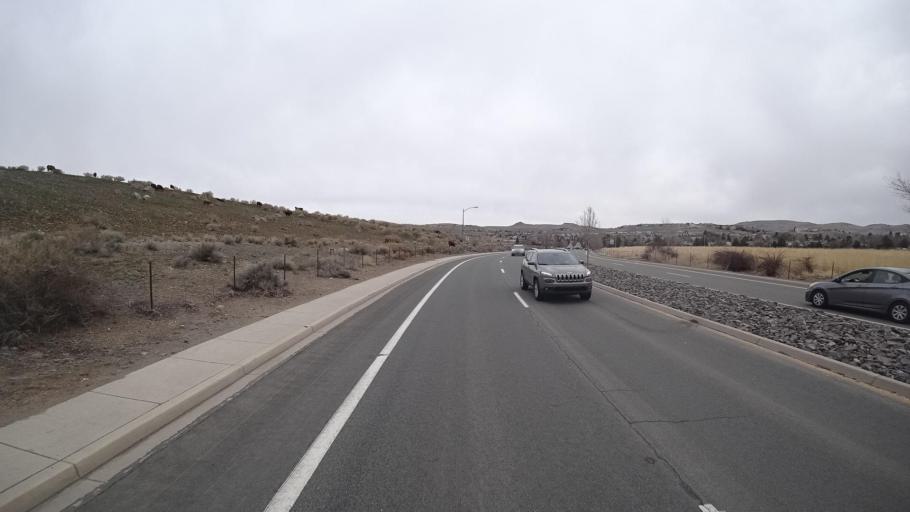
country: US
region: Nevada
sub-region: Washoe County
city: Sparks
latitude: 39.5766
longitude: -119.7281
